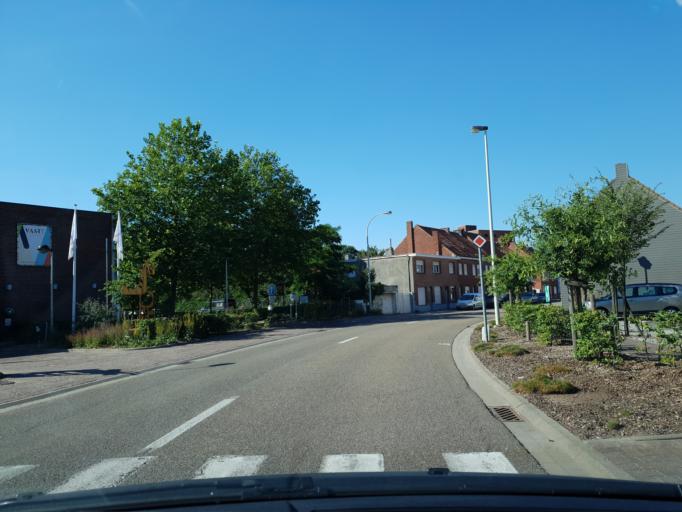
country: BE
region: Flanders
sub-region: Provincie Antwerpen
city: Beerse
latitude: 51.3259
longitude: 4.8549
